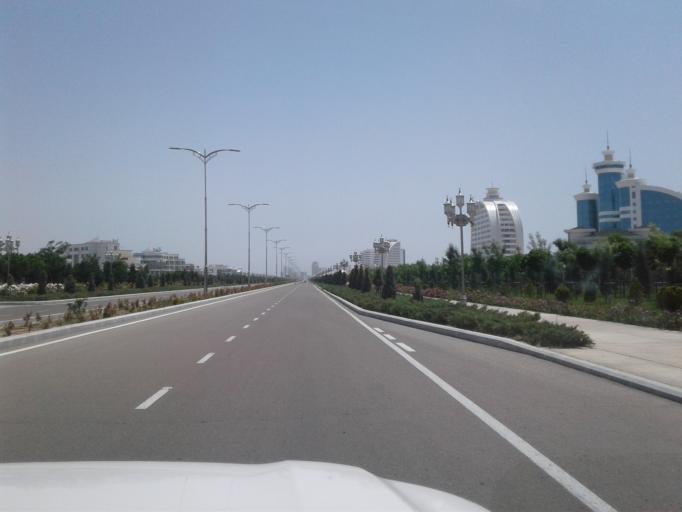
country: TM
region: Balkan
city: Turkmenbasy
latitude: 39.9844
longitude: 52.8254
